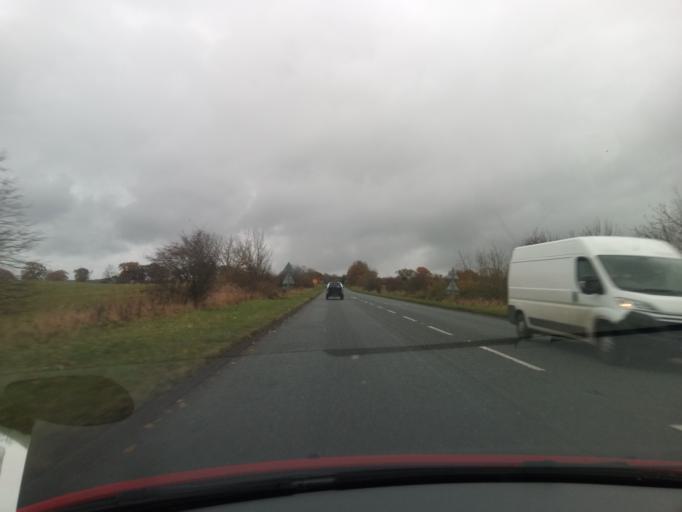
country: GB
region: England
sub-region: County Durham
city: High Etherley
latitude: 54.6598
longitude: -1.7718
